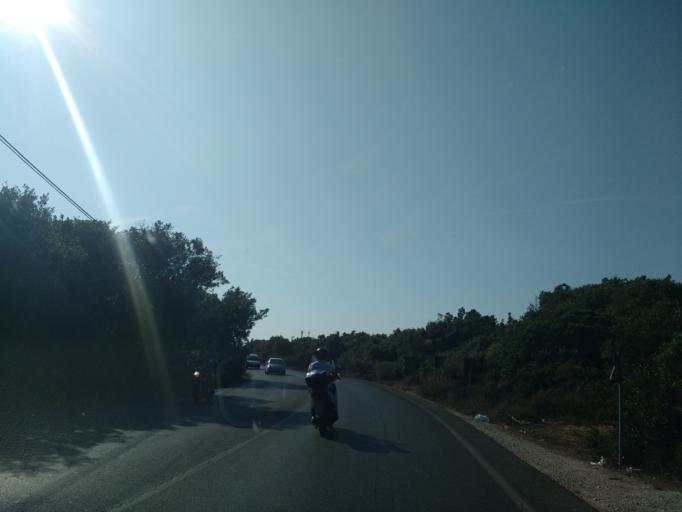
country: IT
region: Latium
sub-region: Citta metropolitana di Roma Capitale
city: Acilia-Castel Fusano-Ostia Antica
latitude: 41.6994
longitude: 12.3545
